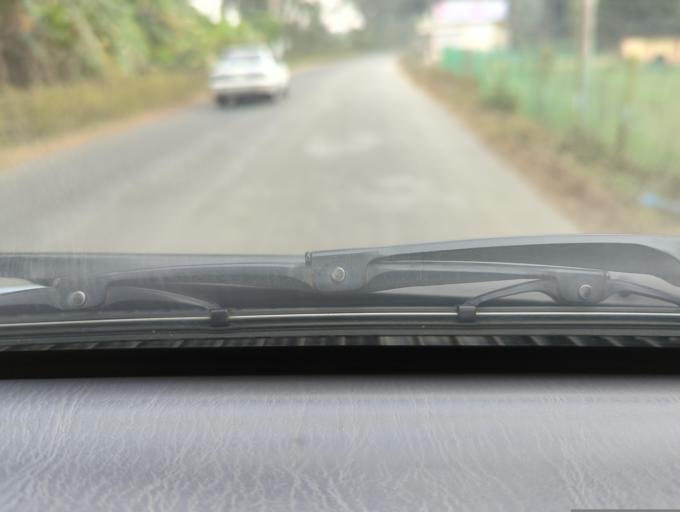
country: BD
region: Sylhet
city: Maulavi Bazar
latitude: 24.5073
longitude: 91.7321
